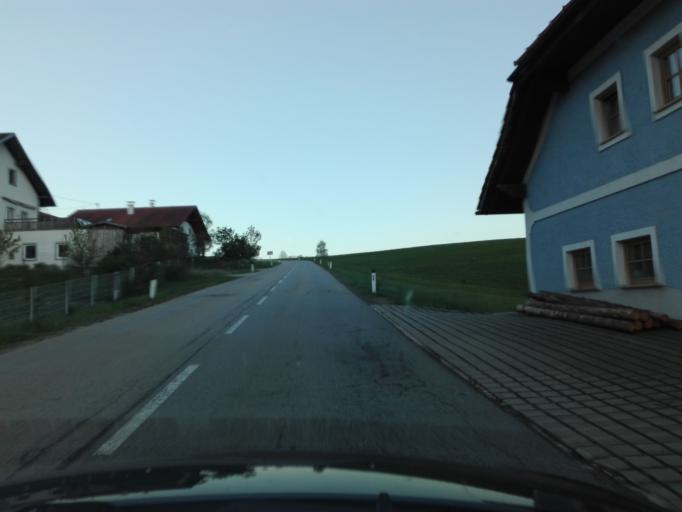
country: DE
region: Bavaria
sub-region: Lower Bavaria
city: Wegscheid
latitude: 48.5485
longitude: 13.7780
